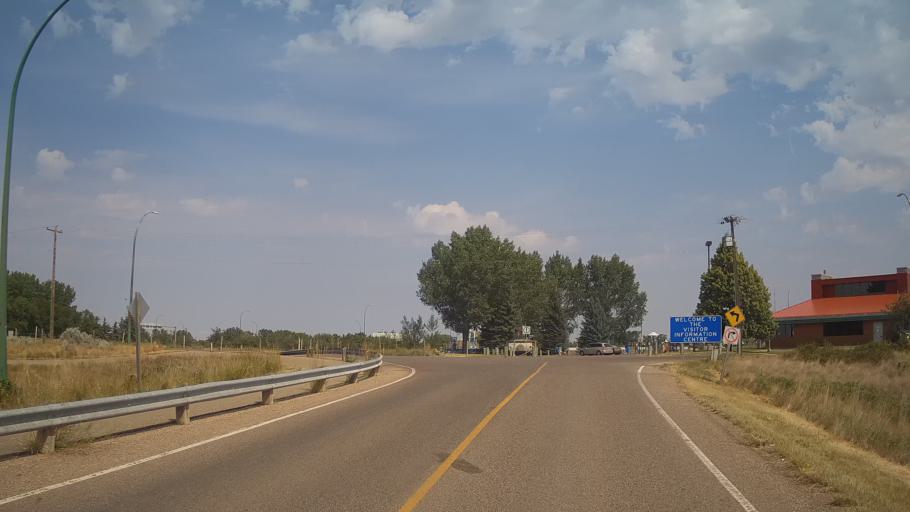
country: CA
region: Alberta
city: Medicine Hat
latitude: 50.0114
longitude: -110.6852
